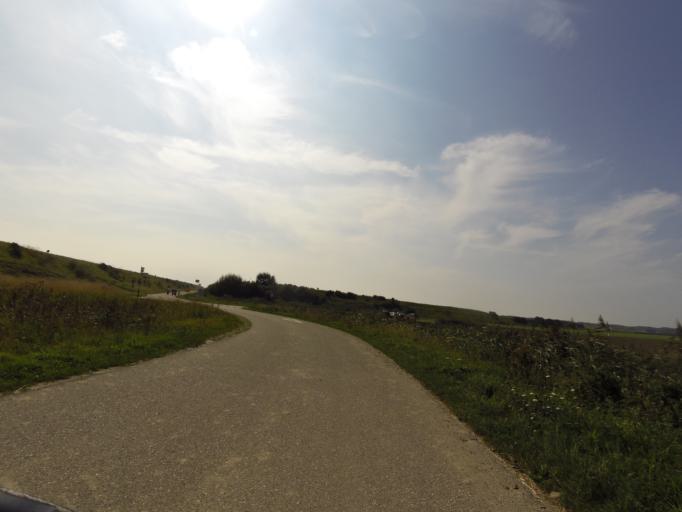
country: NL
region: Zeeland
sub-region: Schouwen-Duiveland
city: Burgh
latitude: 51.6720
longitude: 3.7238
